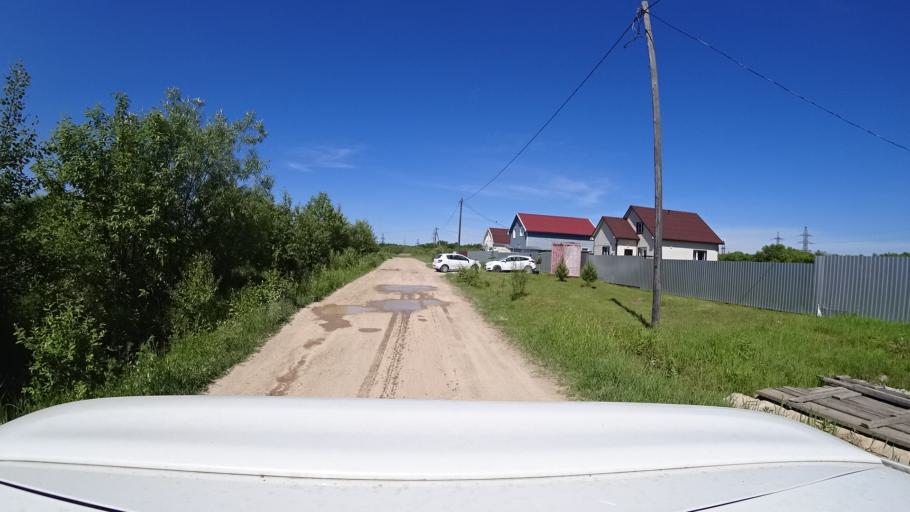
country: RU
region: Khabarovsk Krai
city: Topolevo
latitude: 48.5638
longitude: 135.1934
